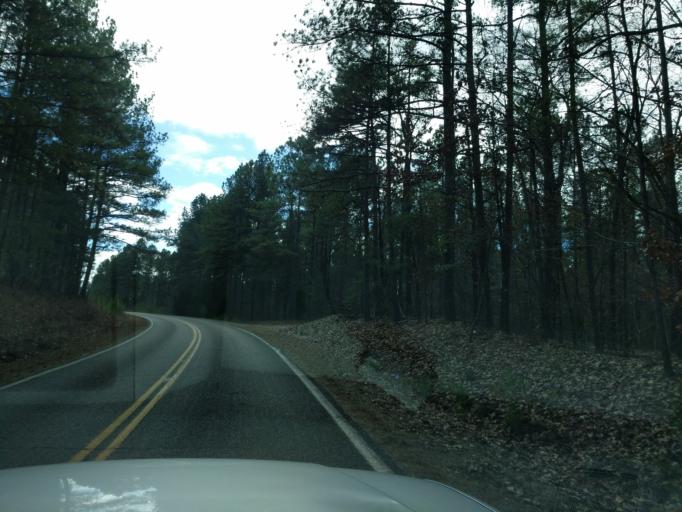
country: US
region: South Carolina
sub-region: Edgefield County
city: Edgefield
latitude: 33.8784
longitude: -81.9982
